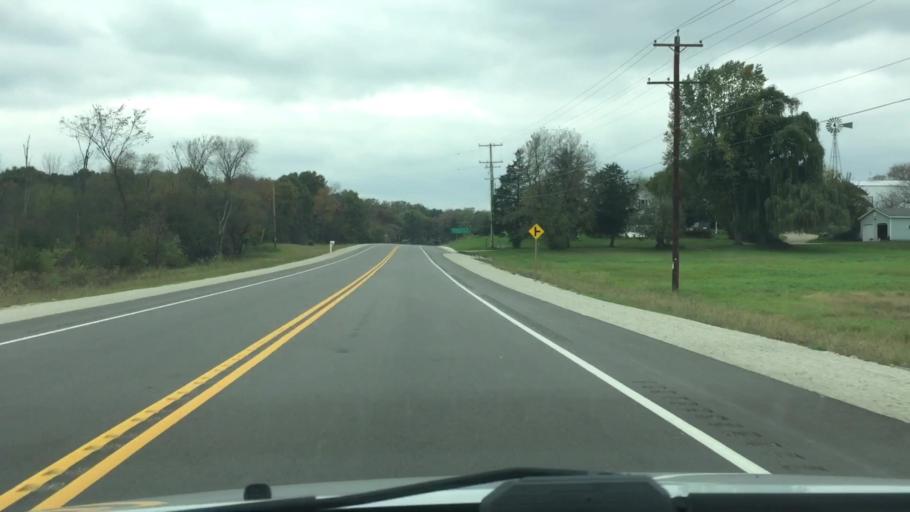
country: US
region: Wisconsin
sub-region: Walworth County
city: Whitewater
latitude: 42.8535
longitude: -88.7911
